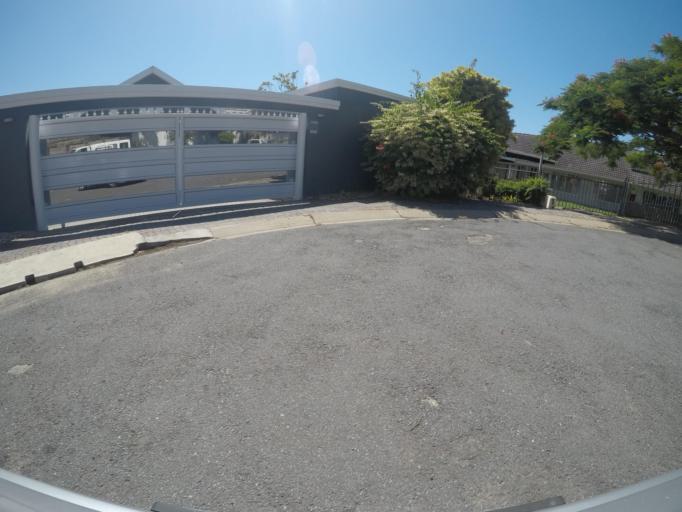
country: ZA
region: Eastern Cape
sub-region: Buffalo City Metropolitan Municipality
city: East London
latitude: -32.9700
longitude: 27.9200
